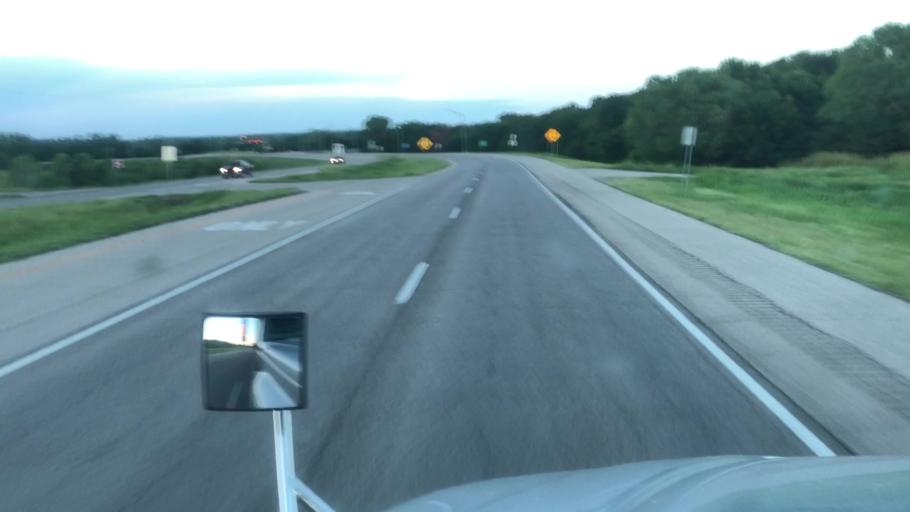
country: US
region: Oklahoma
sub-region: Kay County
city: Ponca City
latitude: 36.6765
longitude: -97.0716
